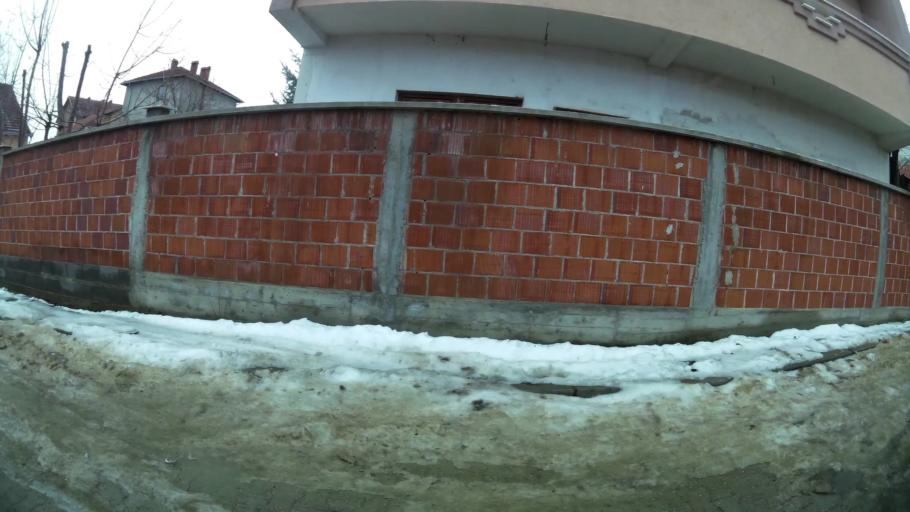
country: XK
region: Pristina
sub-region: Komuna e Prishtines
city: Pristina
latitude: 42.6883
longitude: 21.1720
